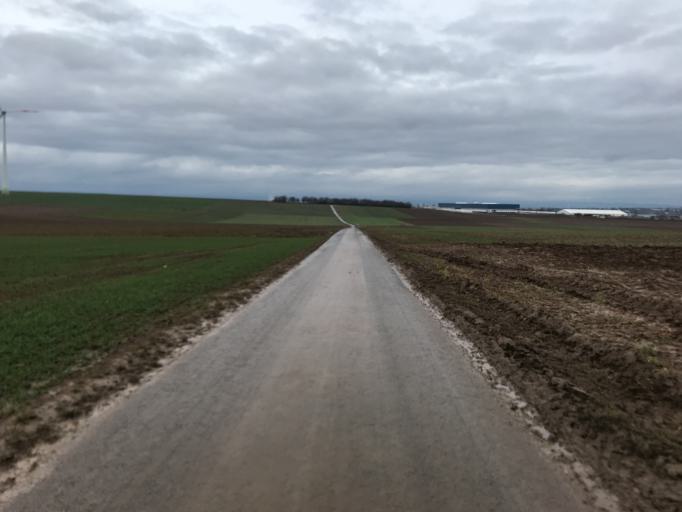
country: DE
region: Rheinland-Pfalz
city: Gau-Bischofsheim
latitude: 49.9316
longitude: 8.2495
